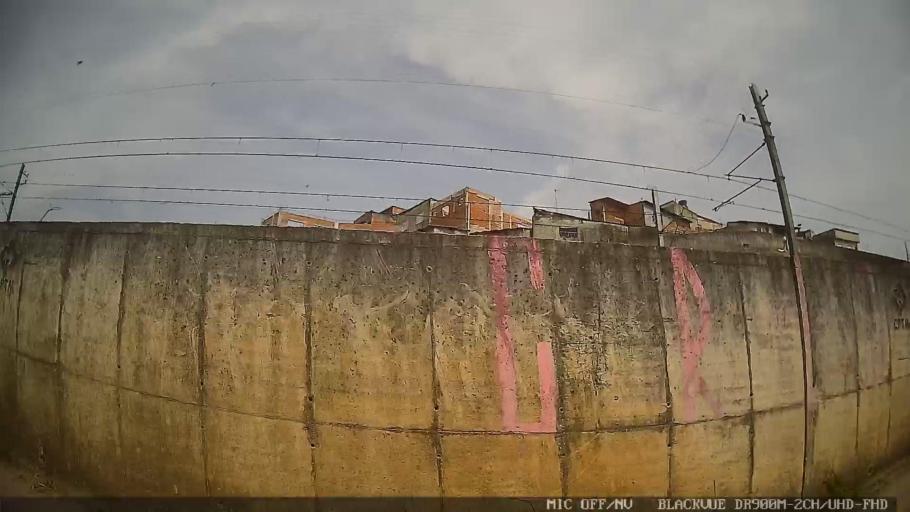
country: BR
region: Sao Paulo
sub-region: Itaquaquecetuba
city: Itaquaquecetuba
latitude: -23.4939
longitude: -46.3377
